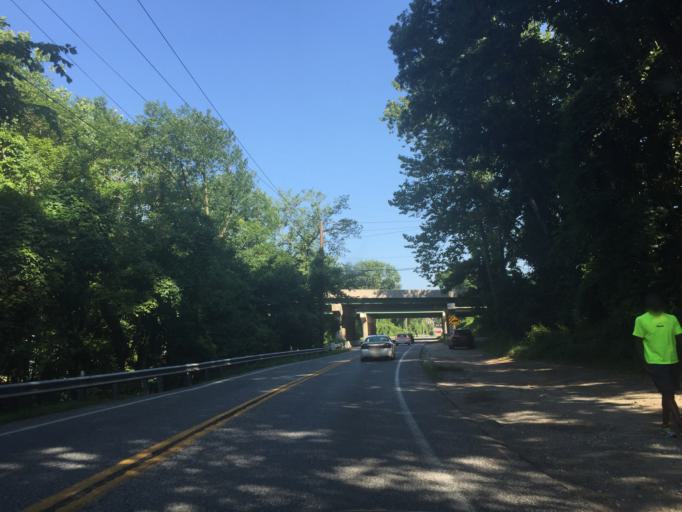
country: US
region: Maryland
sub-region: Baltimore County
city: Mays Chapel
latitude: 39.3967
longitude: -76.6647
